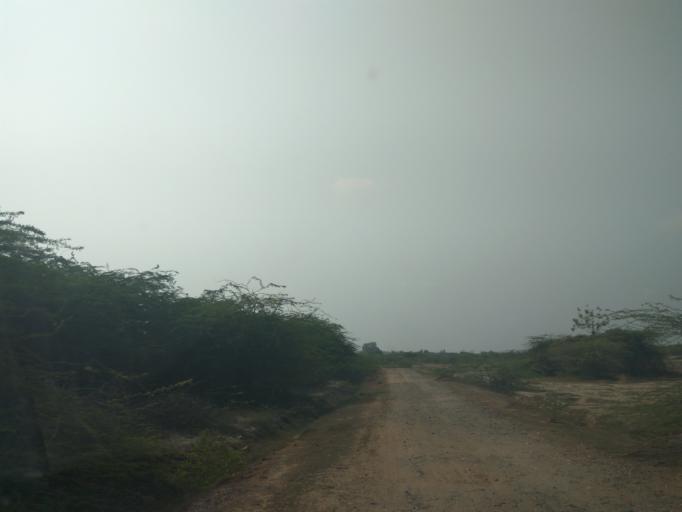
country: IN
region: Andhra Pradesh
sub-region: Prakasam
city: Kandukur
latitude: 15.0777
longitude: 79.6077
